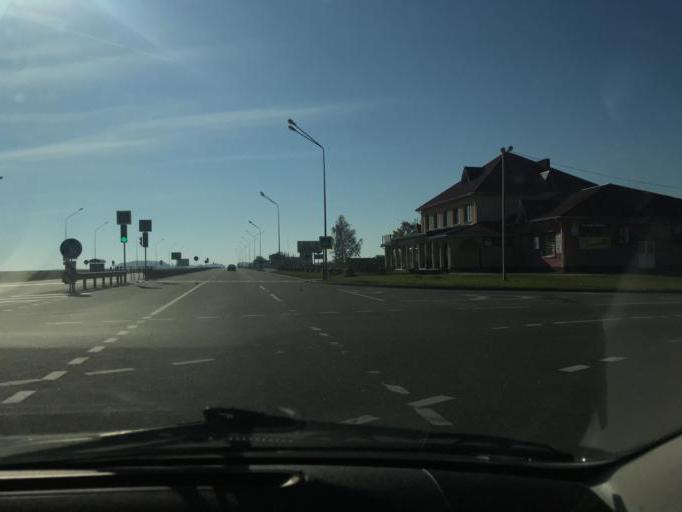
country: BY
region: Minsk
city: Slutsk
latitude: 53.2213
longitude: 27.5505
